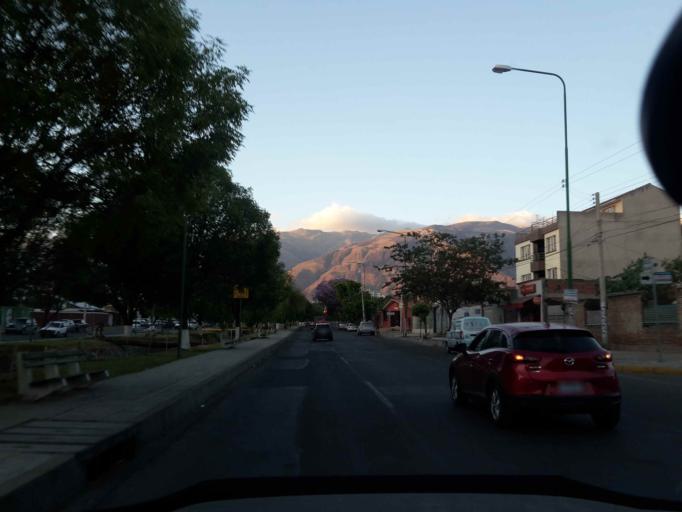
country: BO
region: Cochabamba
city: Cochabamba
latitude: -17.3818
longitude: -66.1815
